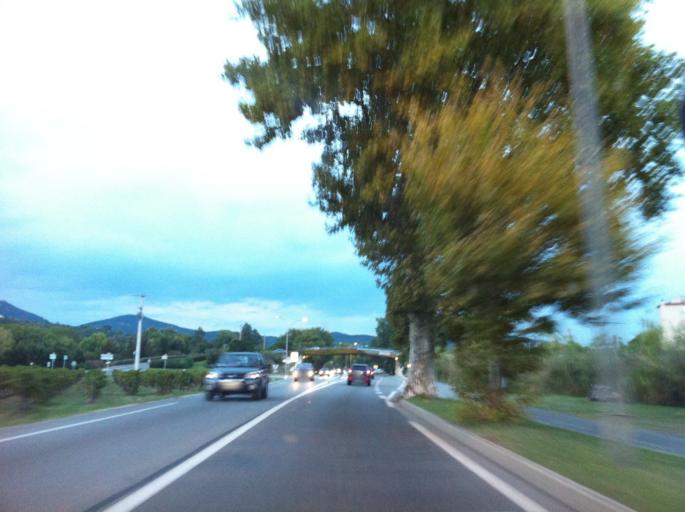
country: FR
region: Provence-Alpes-Cote d'Azur
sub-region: Departement du Var
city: Gassin
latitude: 43.2720
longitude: 6.5736
